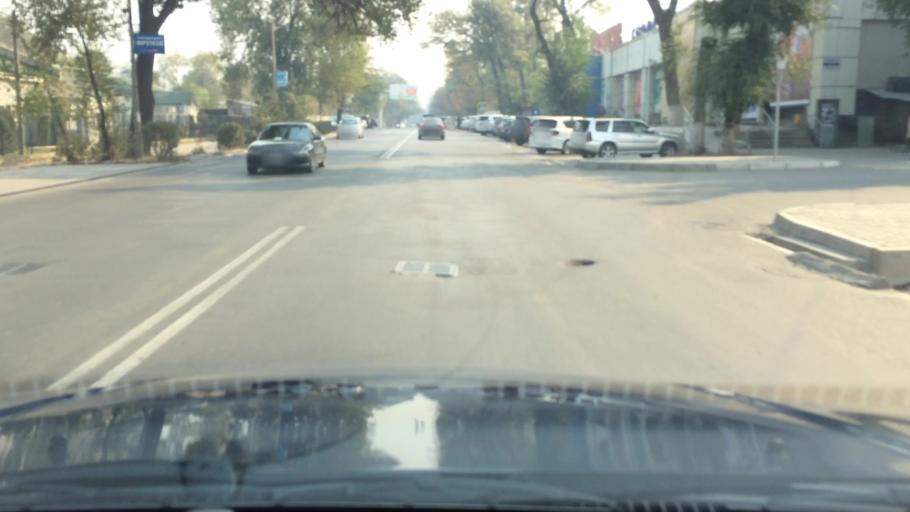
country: KG
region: Chuy
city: Bishkek
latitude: 42.8628
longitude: 74.6033
